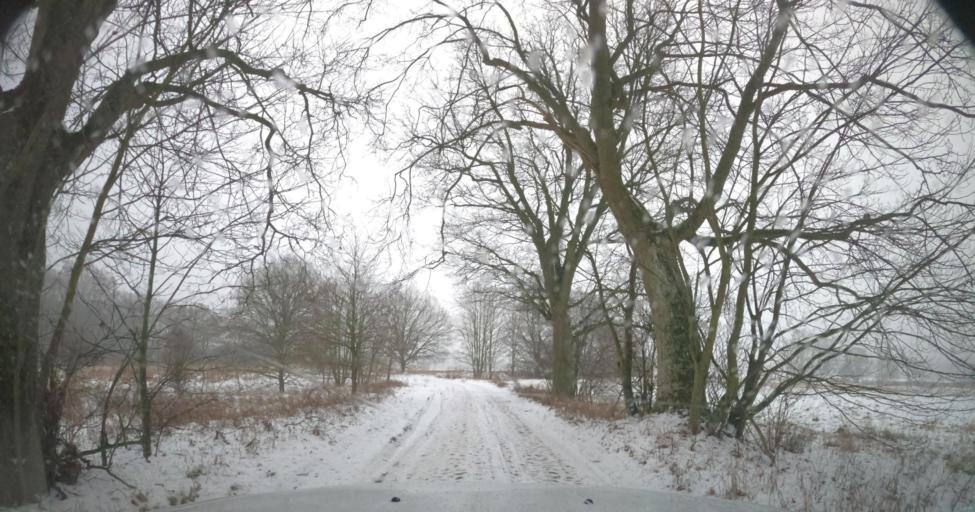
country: PL
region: West Pomeranian Voivodeship
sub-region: Powiat kamienski
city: Golczewo
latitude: 53.7692
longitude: 14.9455
